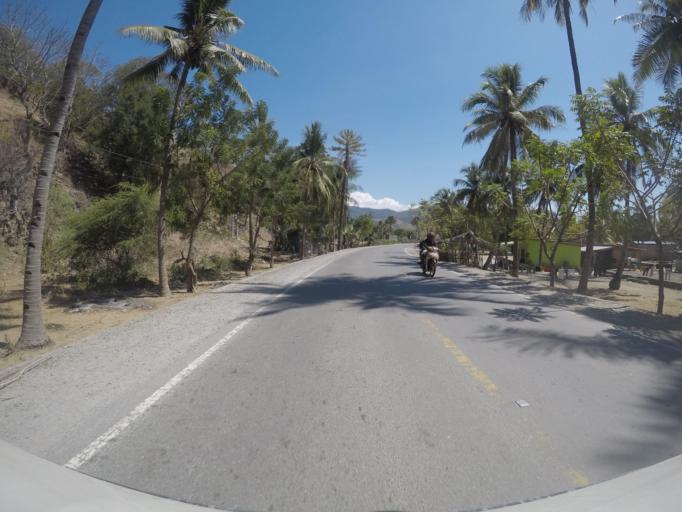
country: TL
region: Dili
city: Dili
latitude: -8.5702
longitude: 125.4662
